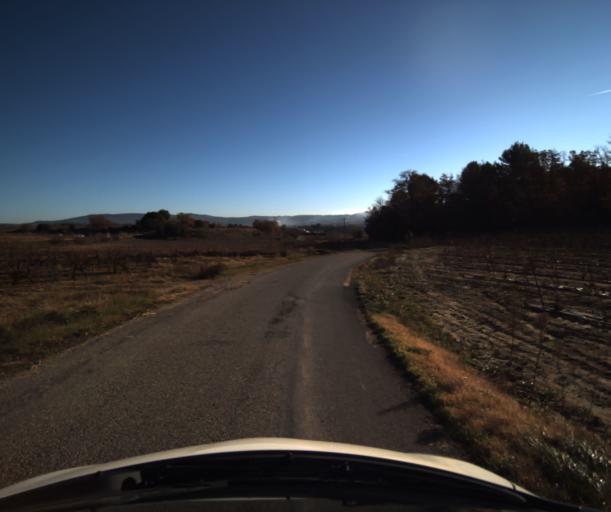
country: FR
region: Provence-Alpes-Cote d'Azur
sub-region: Departement du Vaucluse
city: Pertuis
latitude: 43.7273
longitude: 5.5142
